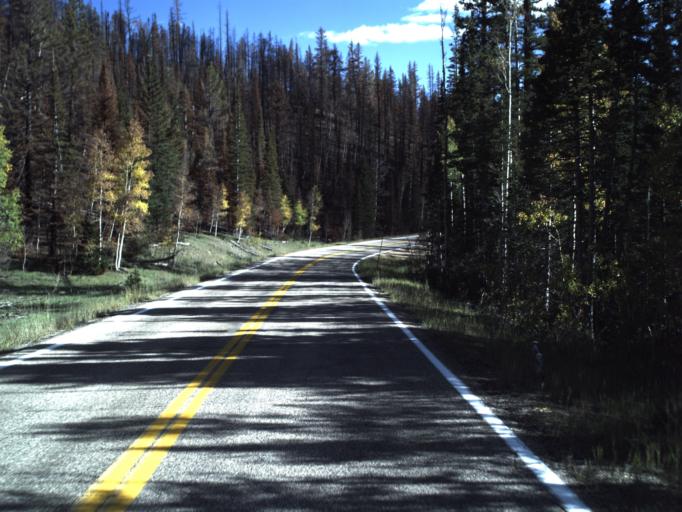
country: US
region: Utah
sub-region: Iron County
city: Parowan
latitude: 37.6598
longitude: -112.7161
